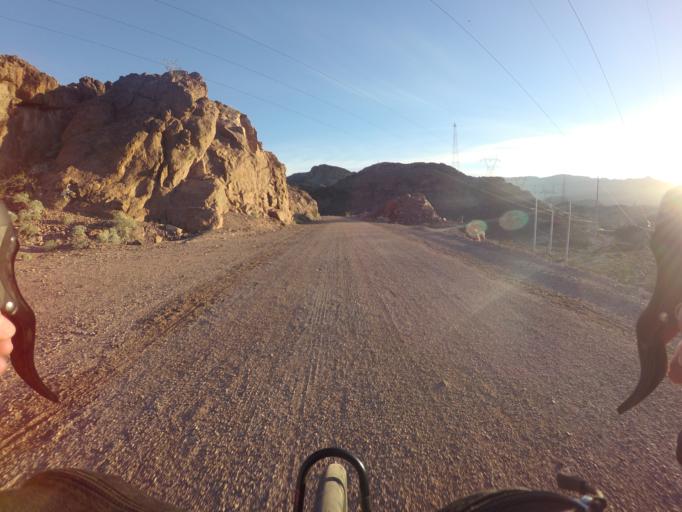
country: US
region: Nevada
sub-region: Clark County
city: Boulder City
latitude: 36.0169
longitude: -114.7513
